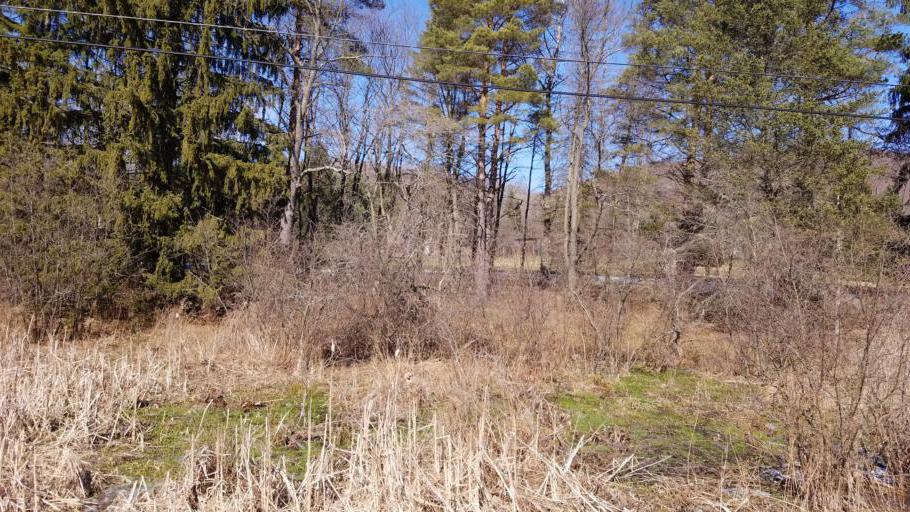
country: US
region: New York
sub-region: Allegany County
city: Wellsville
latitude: 42.0245
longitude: -77.9005
